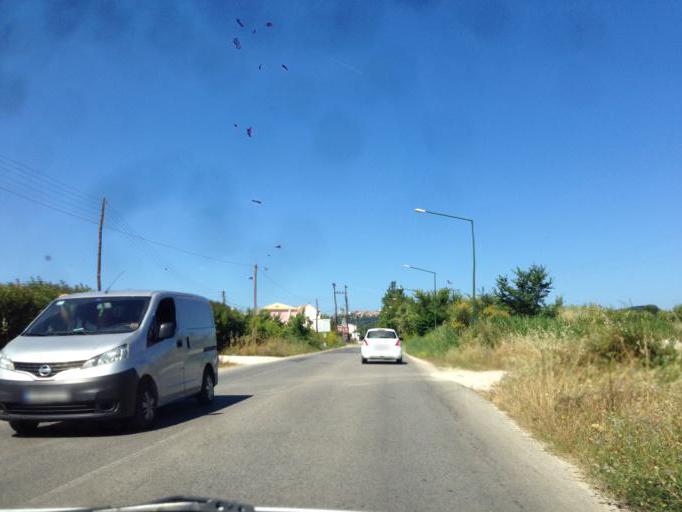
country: GR
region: Ionian Islands
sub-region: Nomos Kerkyras
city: Acharavi
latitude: 39.7859
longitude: 19.7777
